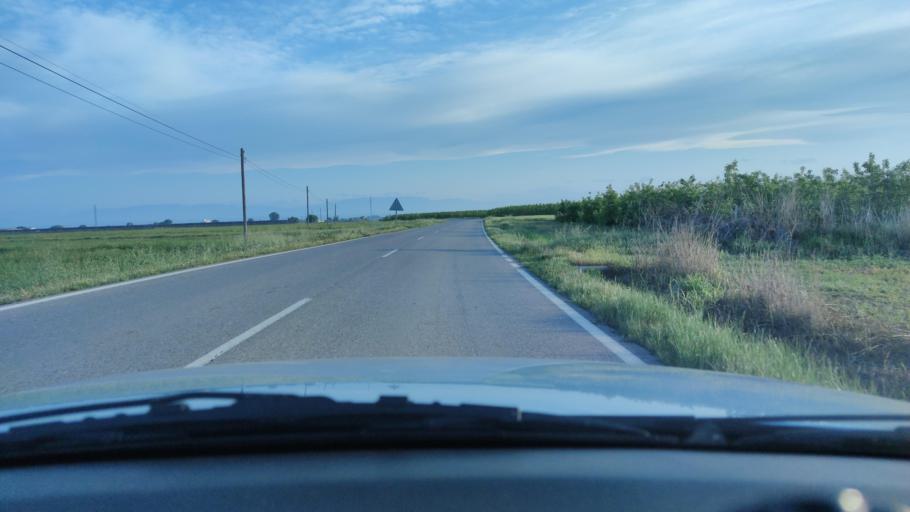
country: ES
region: Catalonia
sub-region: Provincia de Lleida
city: Castellnou de Seana
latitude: 41.6544
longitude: 0.9968
